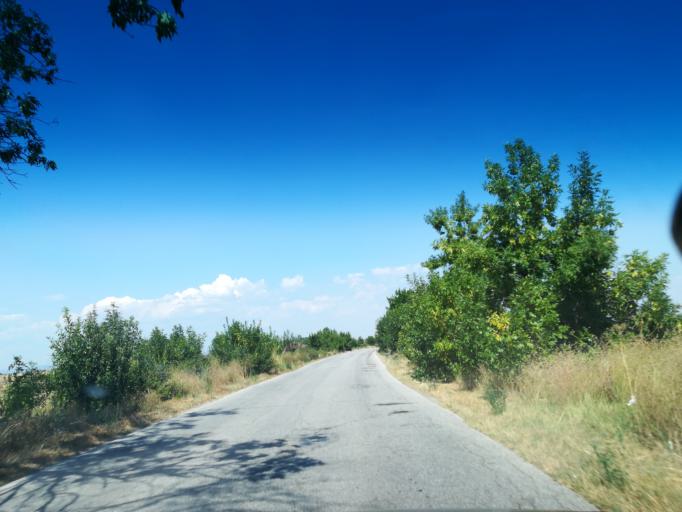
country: BG
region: Stara Zagora
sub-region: Obshtina Chirpan
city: Chirpan
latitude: 42.0582
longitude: 25.1568
